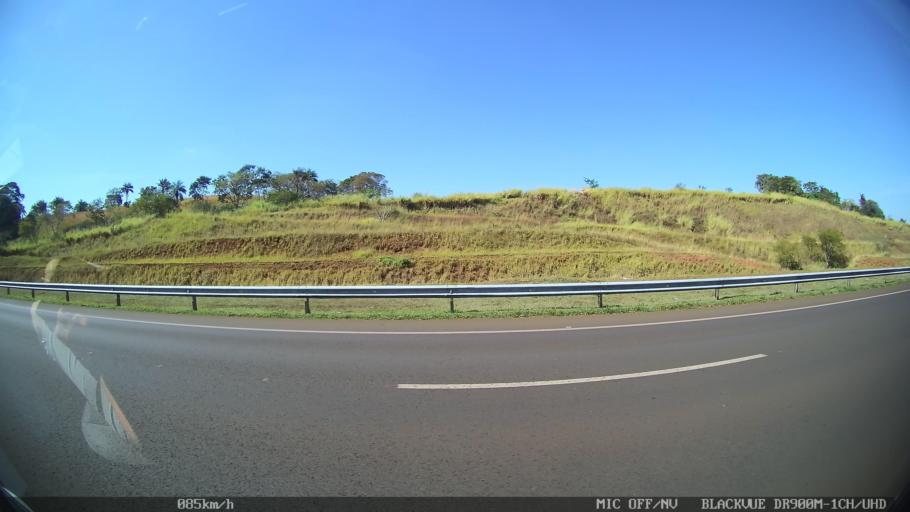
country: BR
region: Sao Paulo
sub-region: Franca
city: Franca
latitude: -20.6091
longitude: -47.4540
